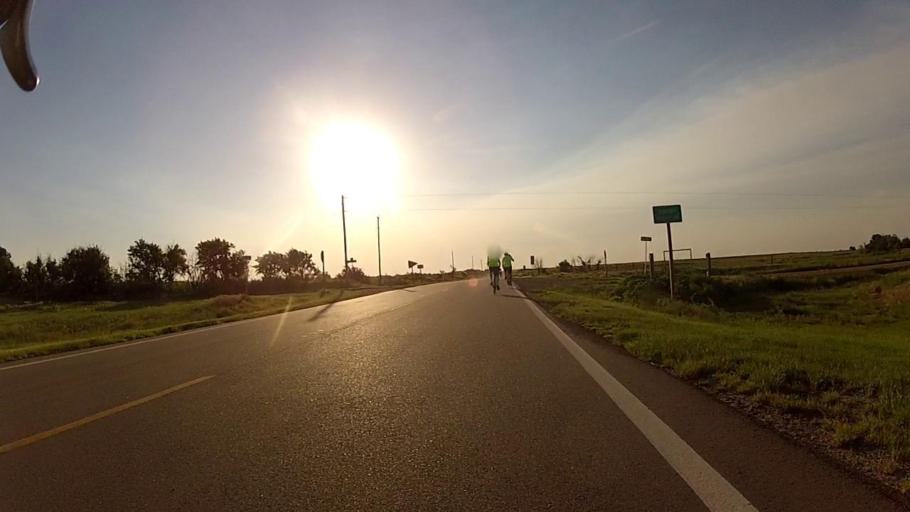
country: US
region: Kansas
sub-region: Harper County
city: Anthony
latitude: 37.1545
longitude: -97.8030
